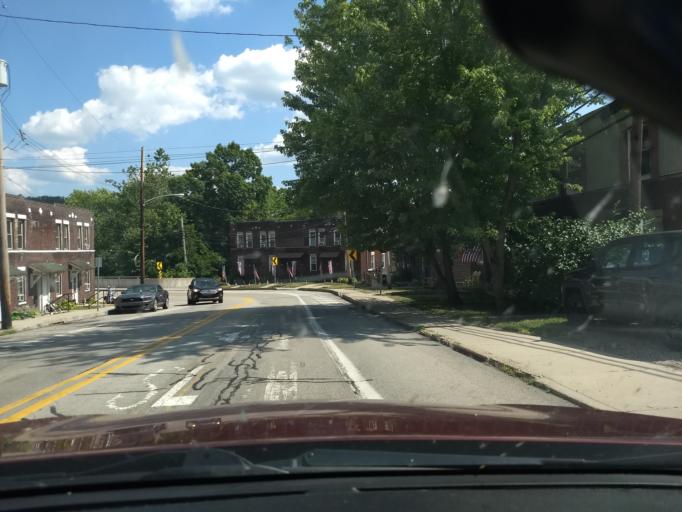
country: US
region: Pennsylvania
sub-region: Westmoreland County
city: Trafford
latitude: 40.3870
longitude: -79.7649
